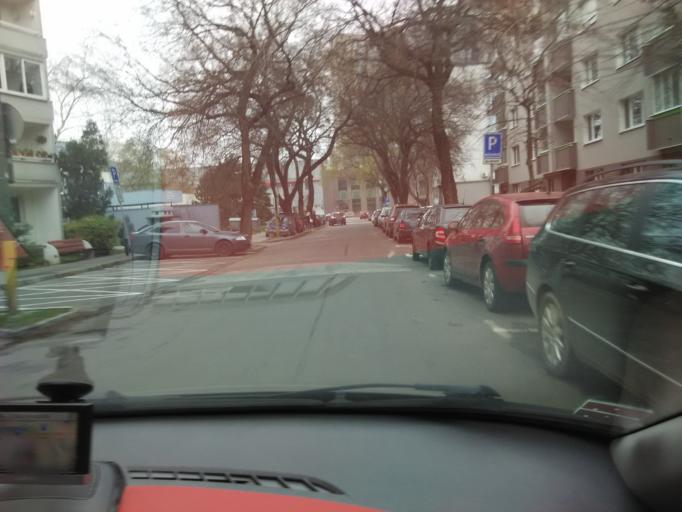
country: SK
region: Bratislavsky
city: Bratislava
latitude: 48.1593
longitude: 17.1391
